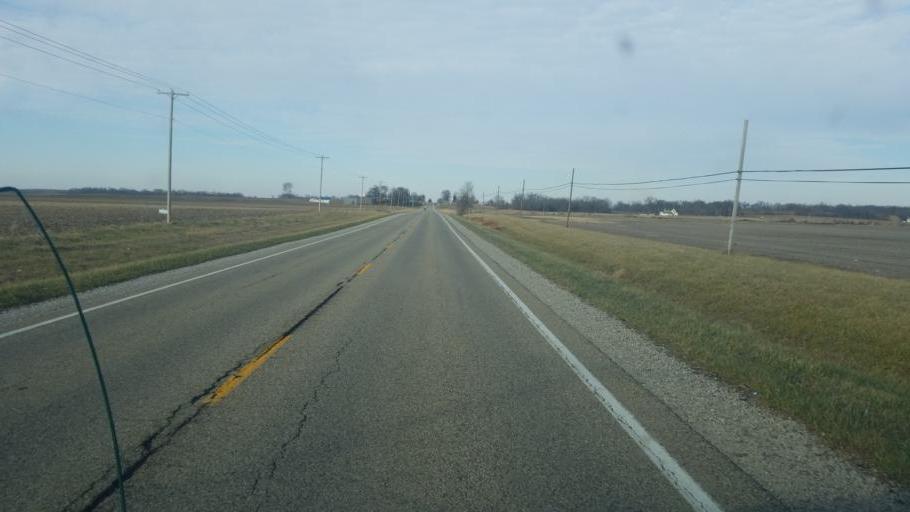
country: US
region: Illinois
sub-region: Lawrence County
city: Bridgeport
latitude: 38.6024
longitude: -87.6943
